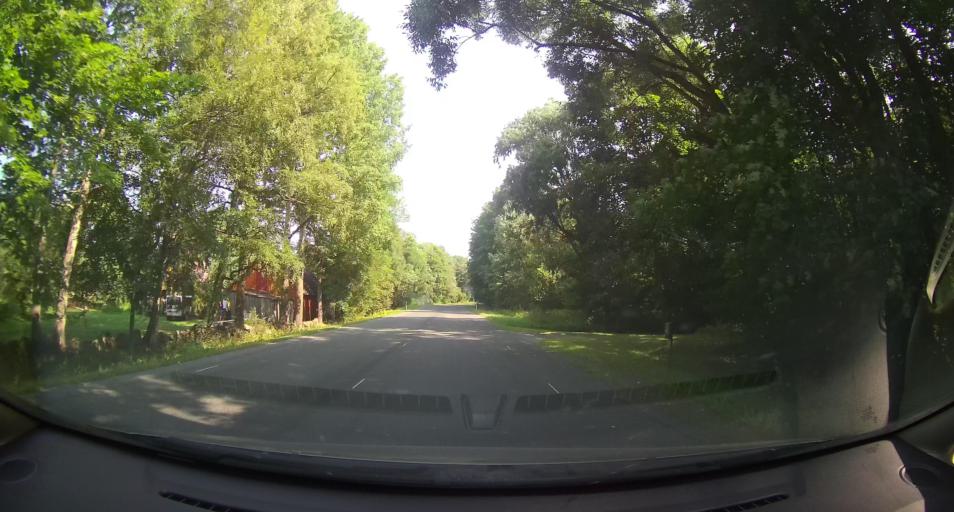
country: EE
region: Paernumaa
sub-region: Audru vald
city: Audru
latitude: 58.4975
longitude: 24.3378
